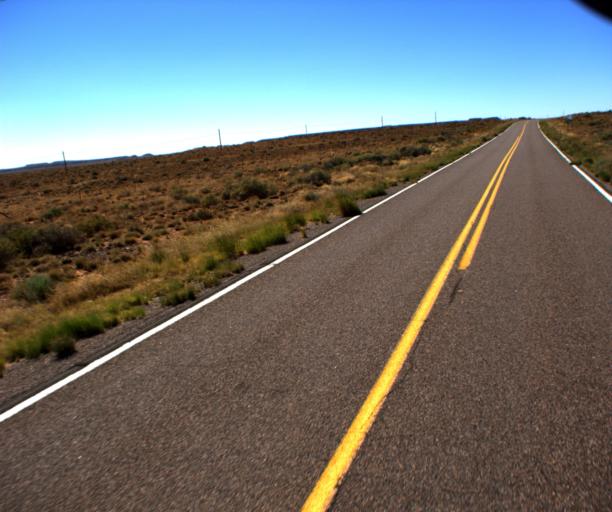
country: US
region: Arizona
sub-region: Coconino County
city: LeChee
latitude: 35.1094
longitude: -110.8666
